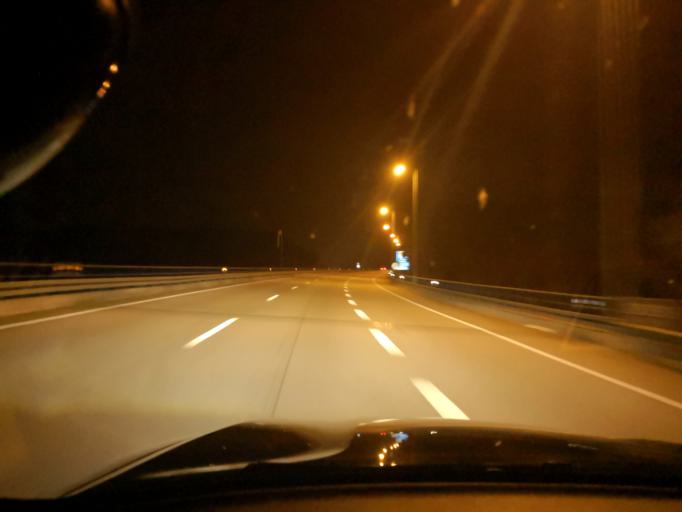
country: PT
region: Aveiro
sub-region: Albergaria-A-Velha
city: Albergaria-a-Velha
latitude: 40.6776
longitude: -8.4450
